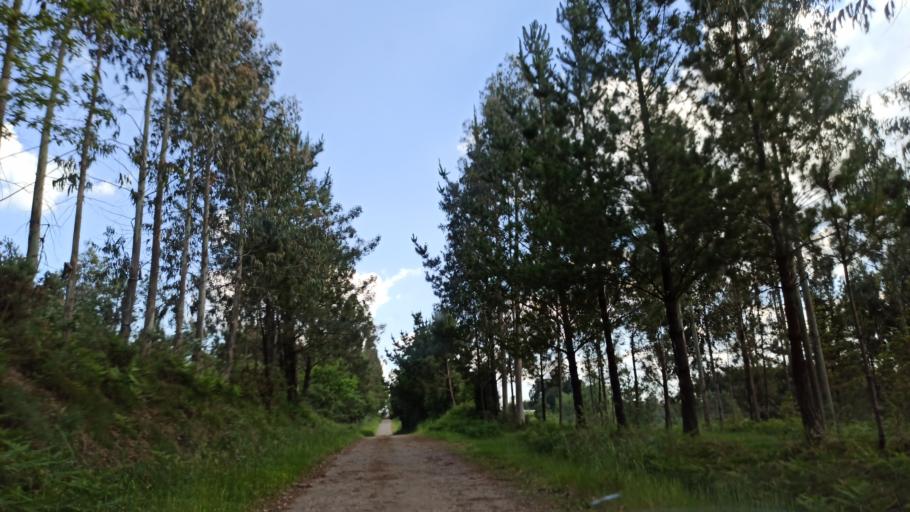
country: ES
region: Galicia
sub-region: Provincia da Coruna
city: Santa Comba
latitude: 43.0788
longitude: -8.7188
